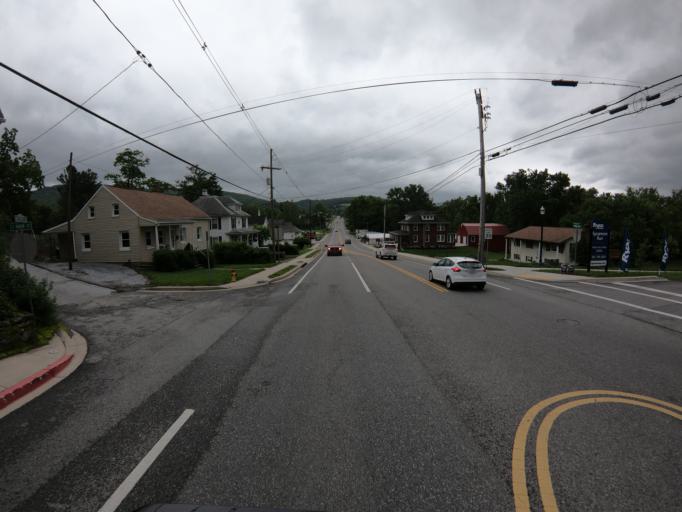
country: US
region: Maryland
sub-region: Washington County
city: Boonsboro
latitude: 39.5010
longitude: -77.6487
